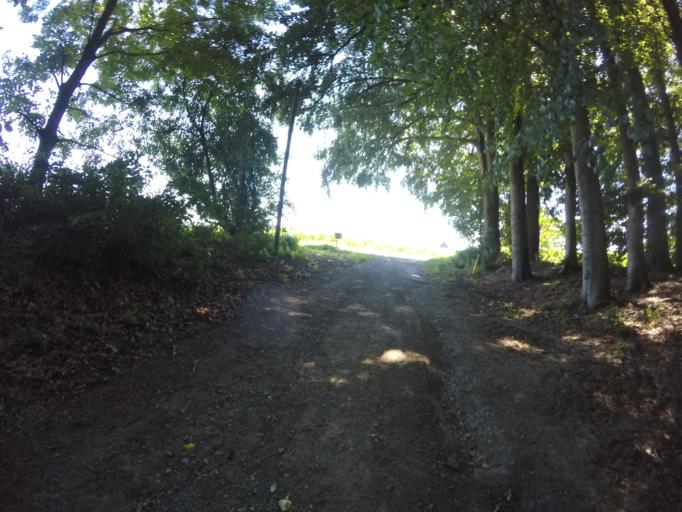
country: DE
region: North Rhine-Westphalia
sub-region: Regierungsbezirk Detmold
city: Herford
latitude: 52.1002
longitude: 8.6120
